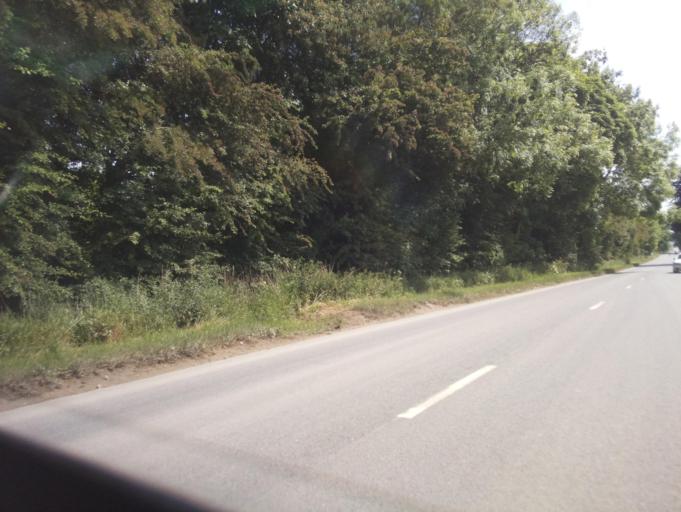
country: GB
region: England
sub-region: North Lincolnshire
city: Manton
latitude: 53.5004
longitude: -0.5748
